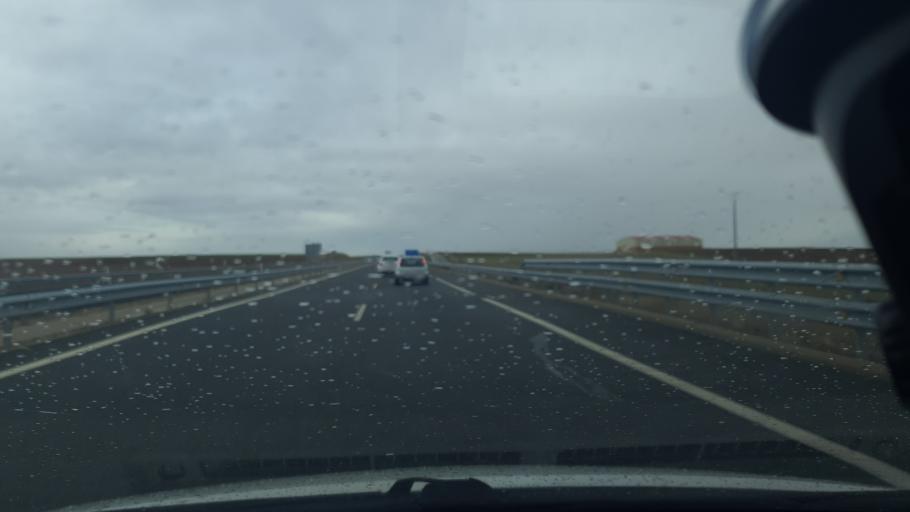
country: ES
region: Castille and Leon
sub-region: Provincia de Segovia
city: Encinillas
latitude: 41.0101
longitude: -4.1647
